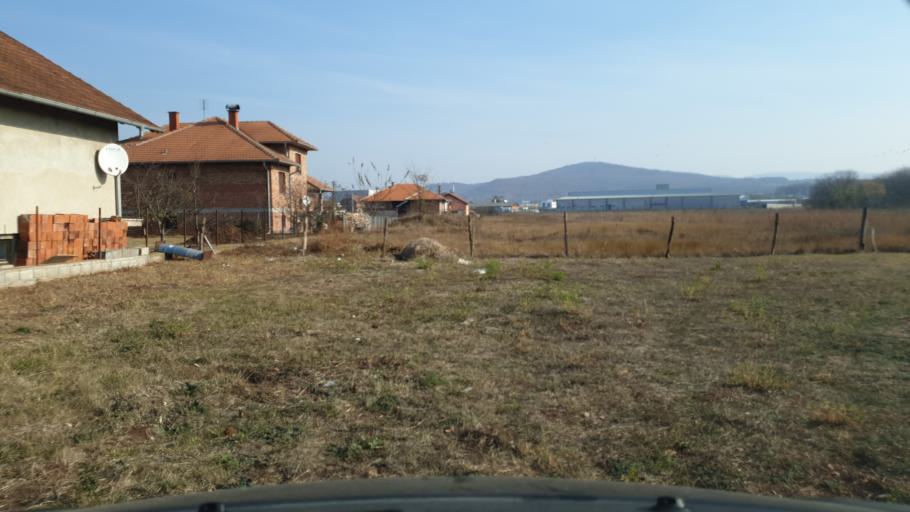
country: RS
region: Central Serbia
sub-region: Pomoravski Okrug
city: Paracin
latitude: 43.8565
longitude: 21.4267
